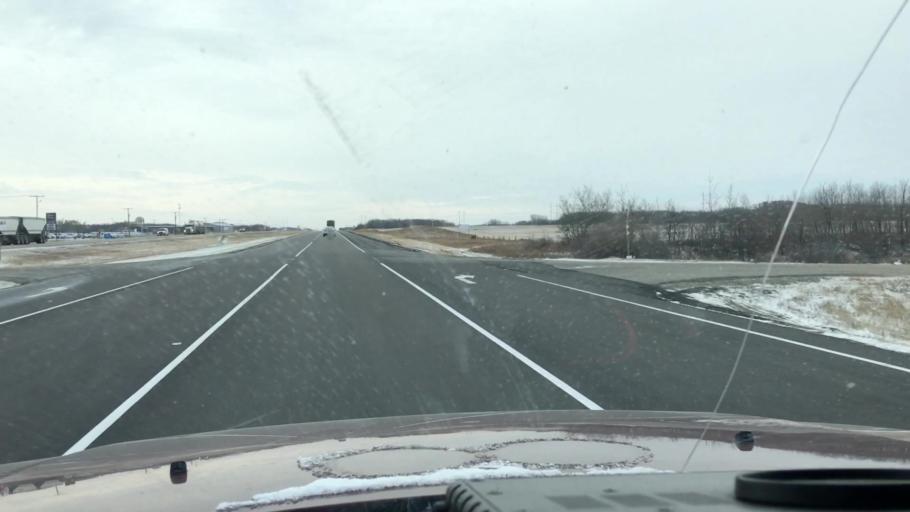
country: CA
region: Saskatchewan
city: Saskatoon
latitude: 51.9693
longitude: -106.5538
